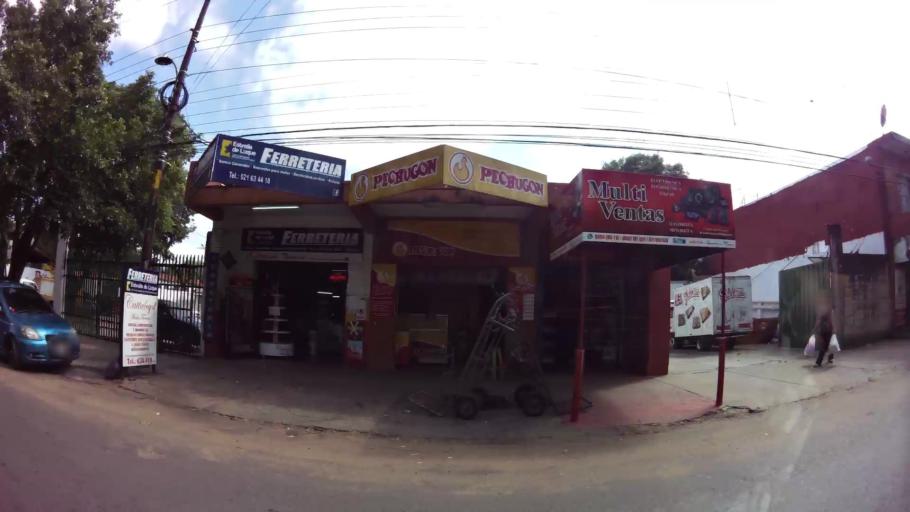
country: PY
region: Central
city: San Lorenzo
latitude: -25.2719
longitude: -57.4906
